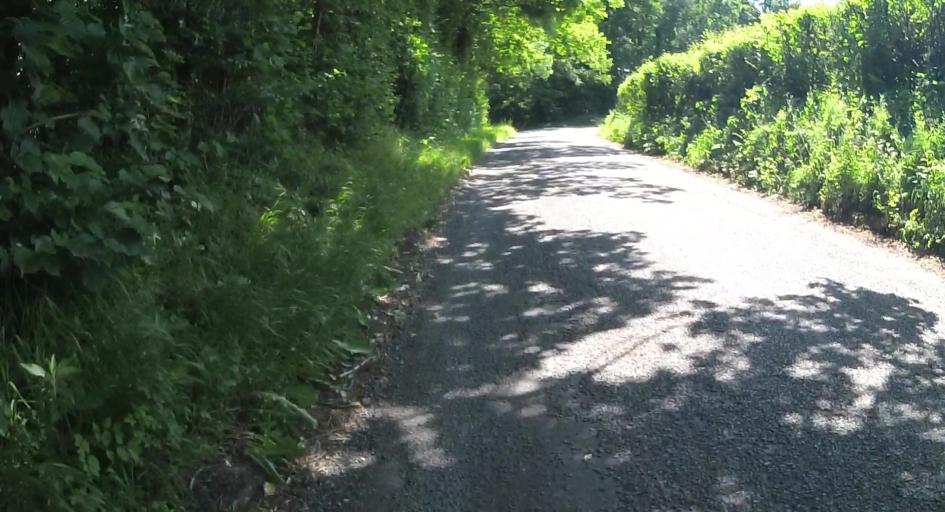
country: GB
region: England
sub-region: West Berkshire
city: Greenham
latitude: 51.3627
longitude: -1.2770
